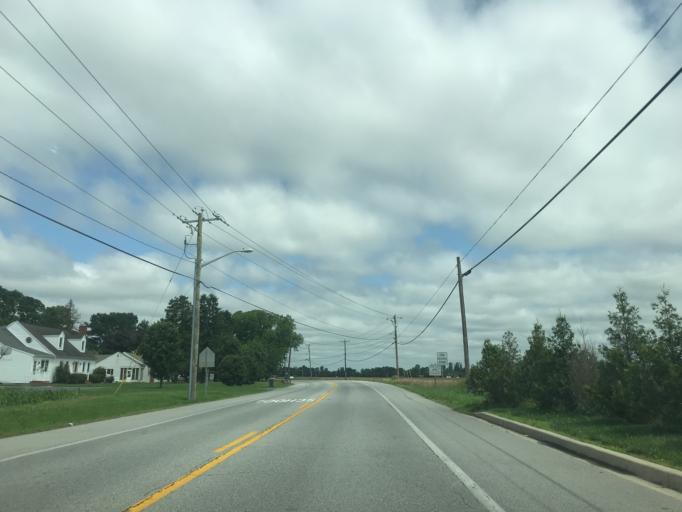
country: US
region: Maryland
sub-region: Caroline County
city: Ridgely
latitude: 38.9534
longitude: -75.8862
